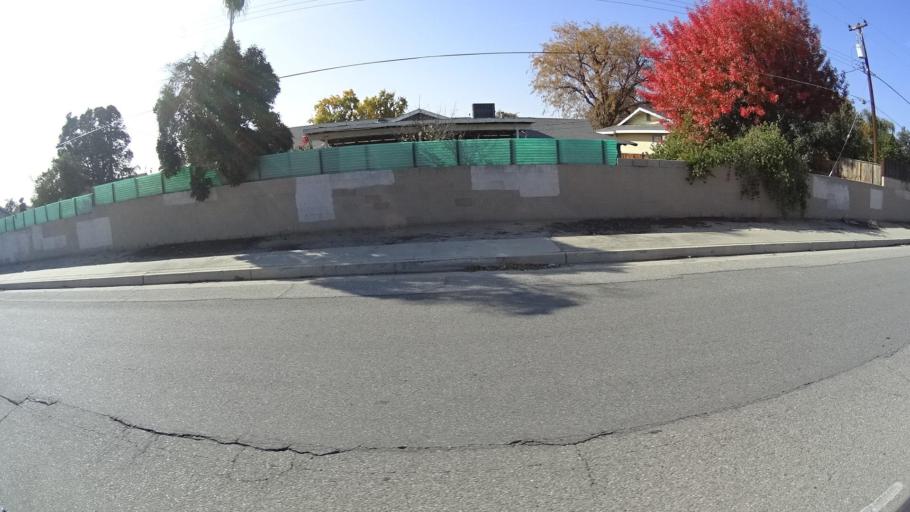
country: US
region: California
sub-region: Kern County
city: Oildale
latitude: 35.4463
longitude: -119.0273
